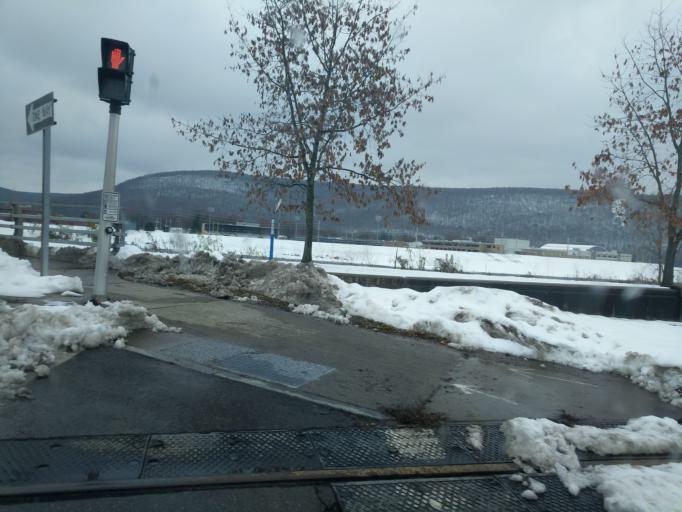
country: US
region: New York
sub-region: Steuben County
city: Corning
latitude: 42.1436
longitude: -77.0520
